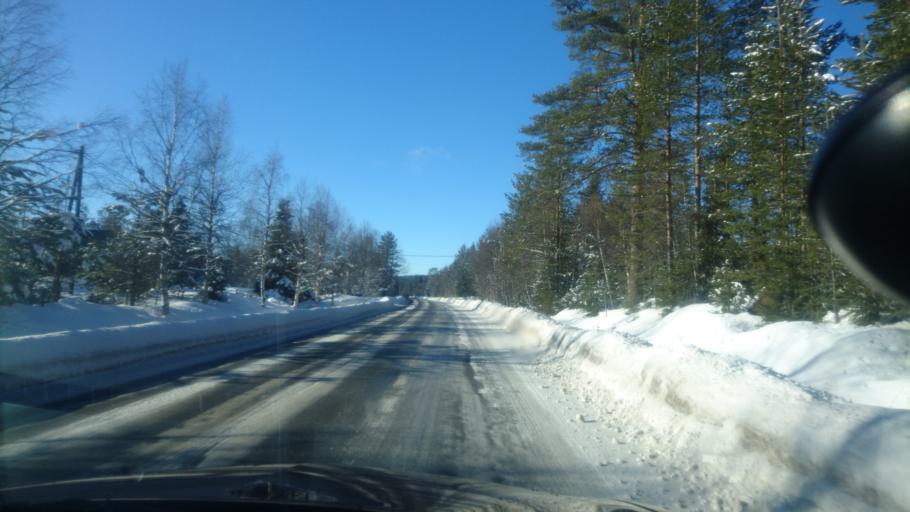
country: NO
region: Hedmark
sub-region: Trysil
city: Innbygda
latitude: 61.2668
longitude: 12.3862
